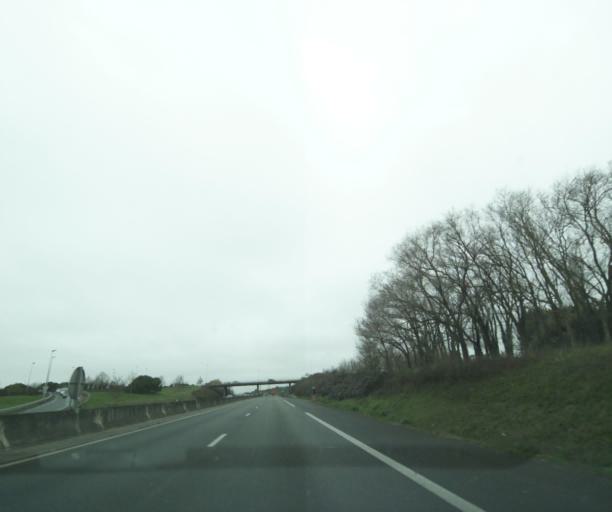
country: FR
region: Poitou-Charentes
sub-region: Departement de la Charente-Maritime
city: Perigny
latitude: 46.1517
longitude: -1.1128
